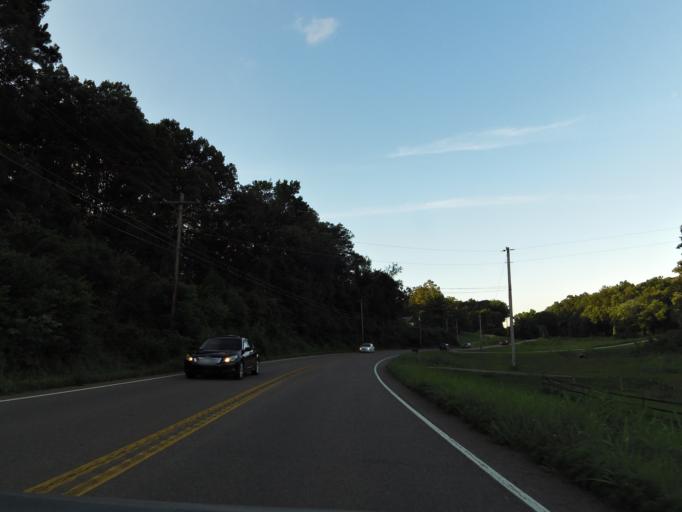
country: US
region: Tennessee
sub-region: Loudon County
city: Lenoir City
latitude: 35.8376
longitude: -84.2369
